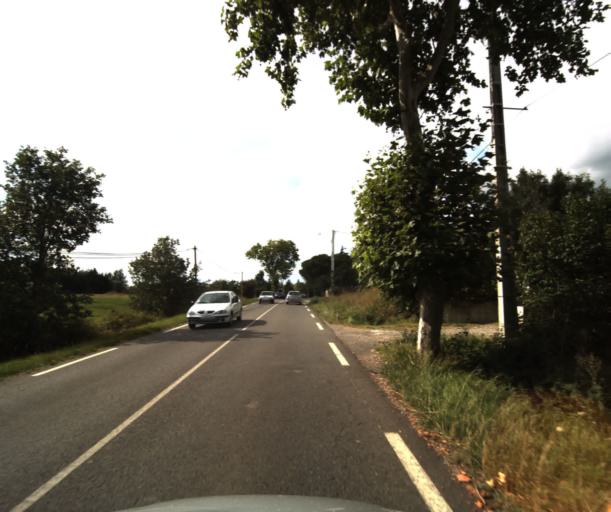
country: FR
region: Midi-Pyrenees
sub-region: Departement de la Haute-Garonne
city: Eaunes
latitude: 43.4412
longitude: 1.3400
